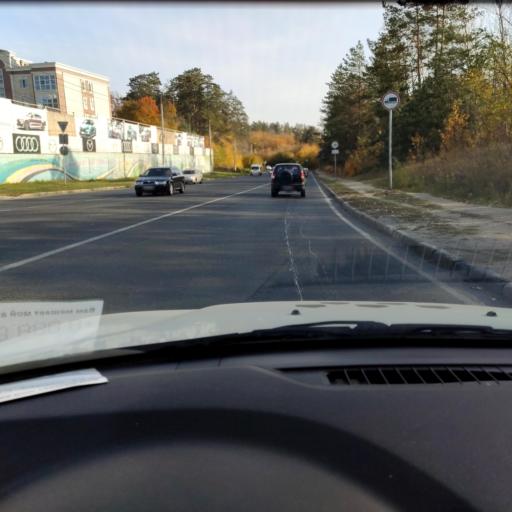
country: RU
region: Samara
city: Tol'yatti
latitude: 53.4953
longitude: 49.2893
